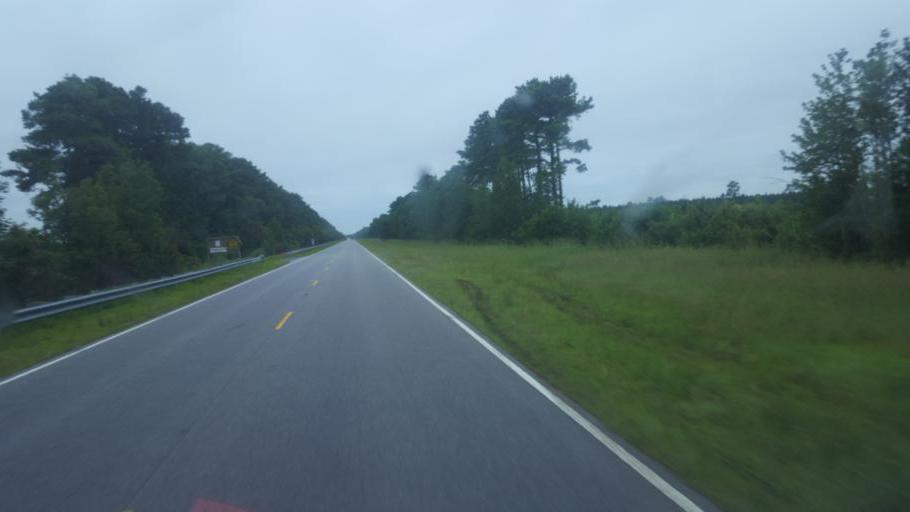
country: US
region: North Carolina
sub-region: Tyrrell County
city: Columbia
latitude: 35.9165
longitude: -76.1220
